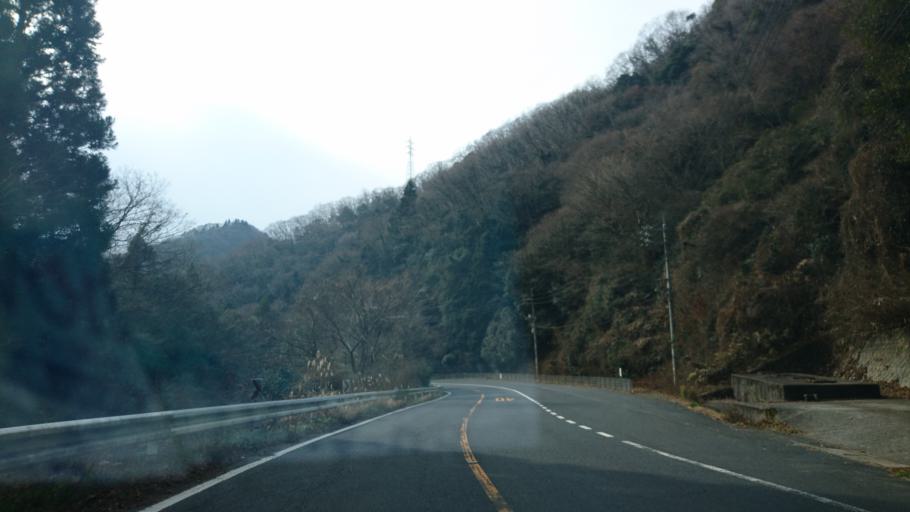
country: JP
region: Okayama
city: Takahashi
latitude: 34.8233
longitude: 133.6535
